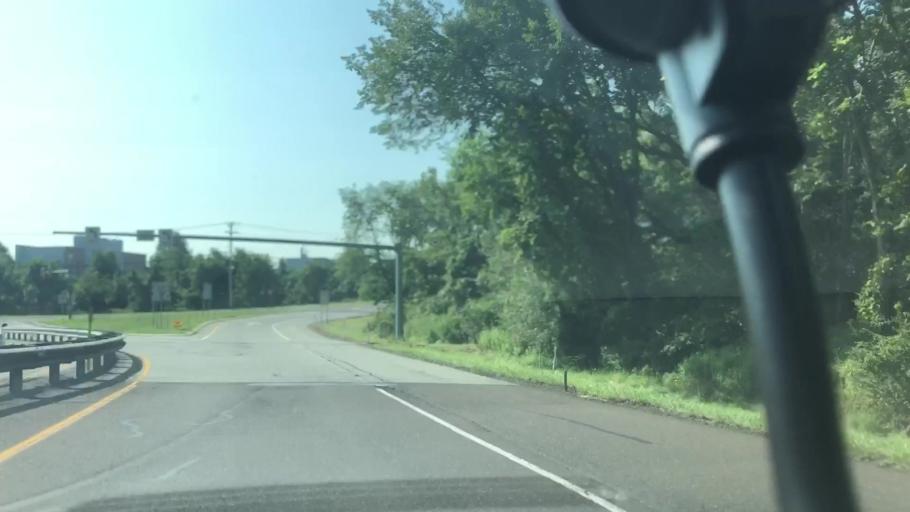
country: US
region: Pennsylvania
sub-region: Montgomery County
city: Trappe
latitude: 40.1605
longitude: -75.4825
